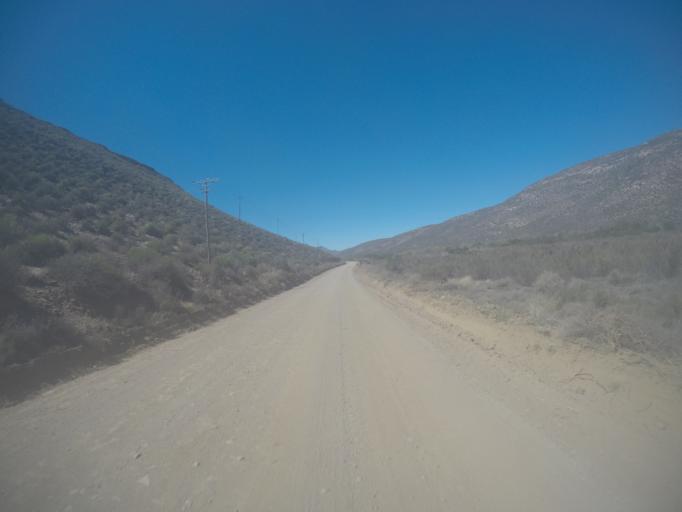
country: ZA
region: Western Cape
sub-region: West Coast District Municipality
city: Clanwilliam
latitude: -32.5083
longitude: 19.3425
